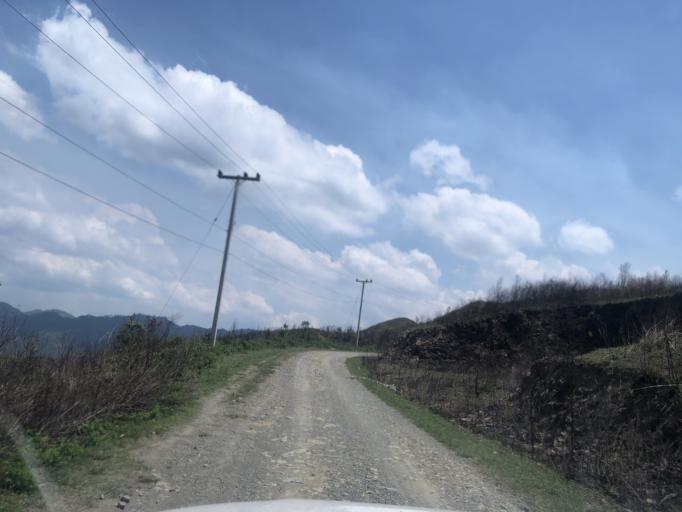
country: LA
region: Phongsali
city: Phongsali
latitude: 21.4166
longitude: 102.1851
